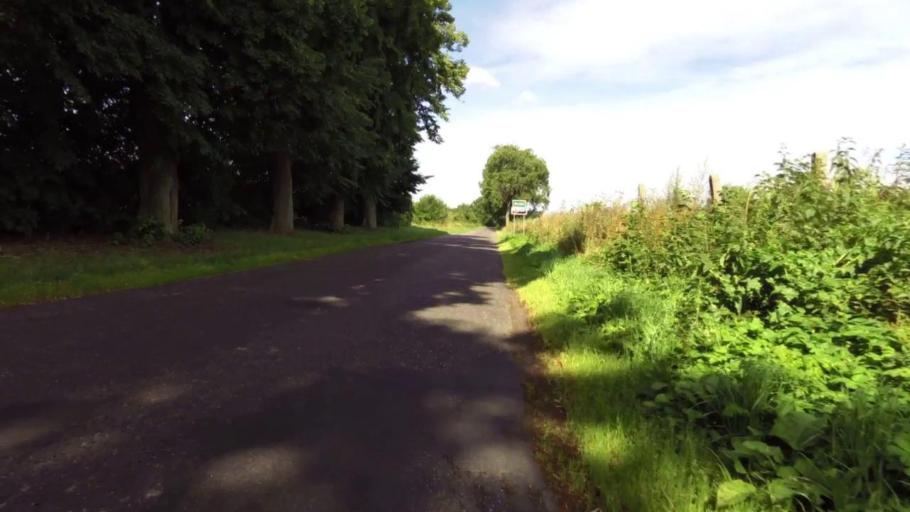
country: PL
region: West Pomeranian Voivodeship
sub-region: Powiat stargardzki
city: Stara Dabrowa
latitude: 53.3400
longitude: 15.1826
